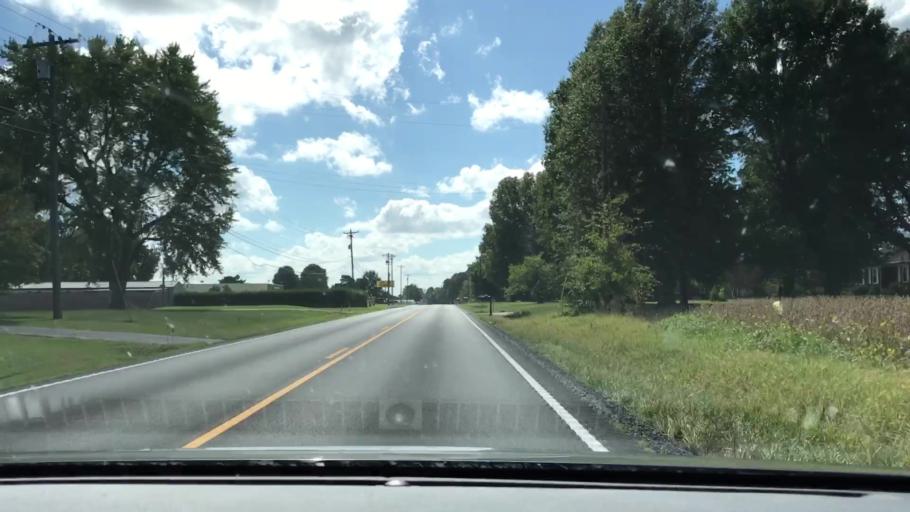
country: US
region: Kentucky
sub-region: Graves County
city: Mayfield
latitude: 36.7650
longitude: -88.5961
